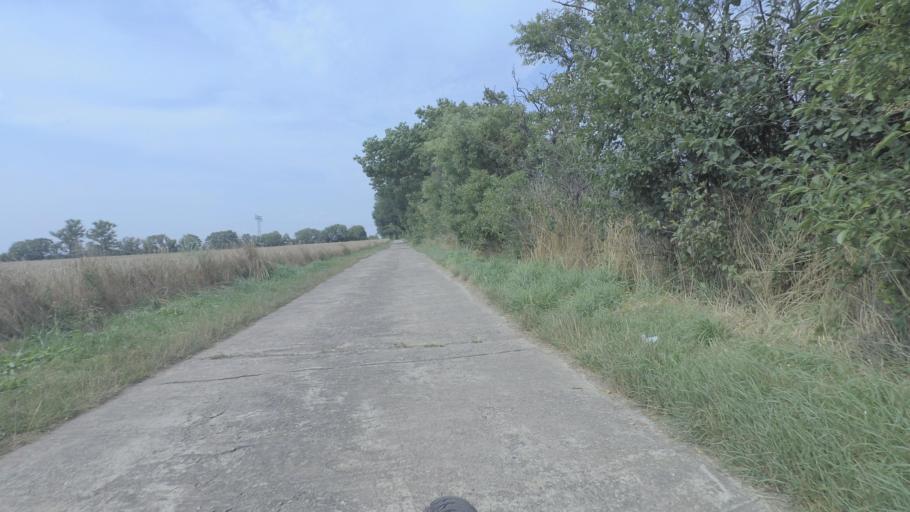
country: DE
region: Brandenburg
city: Rangsdorf
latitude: 52.3345
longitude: 13.4595
